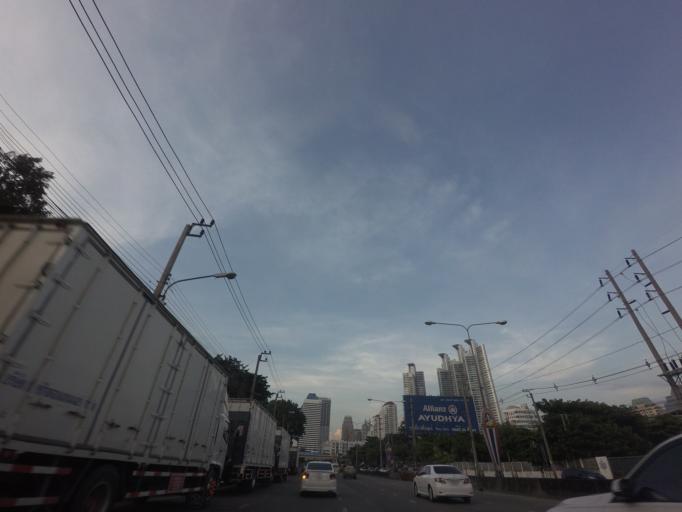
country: TH
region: Bangkok
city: Khlong Toei
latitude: 13.7247
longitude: 100.5604
